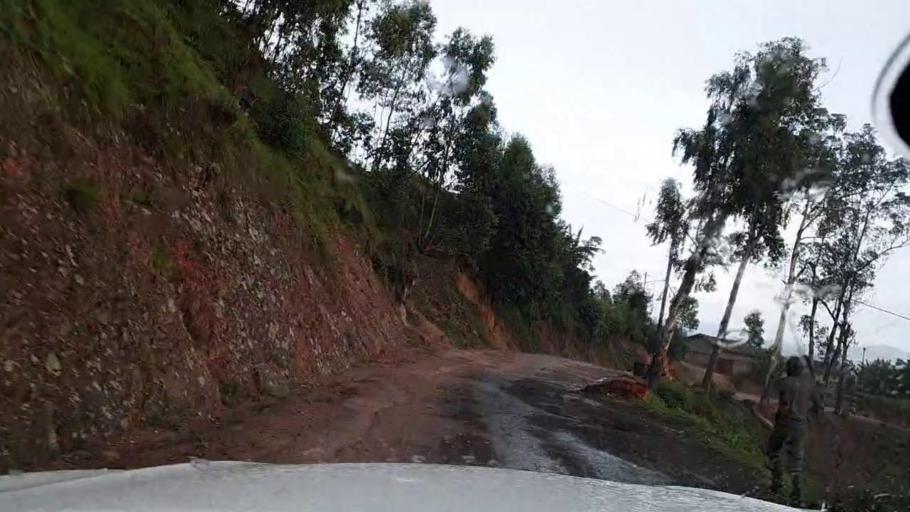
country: BI
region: Kayanza
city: Kayanza
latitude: -2.7764
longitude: 29.5356
